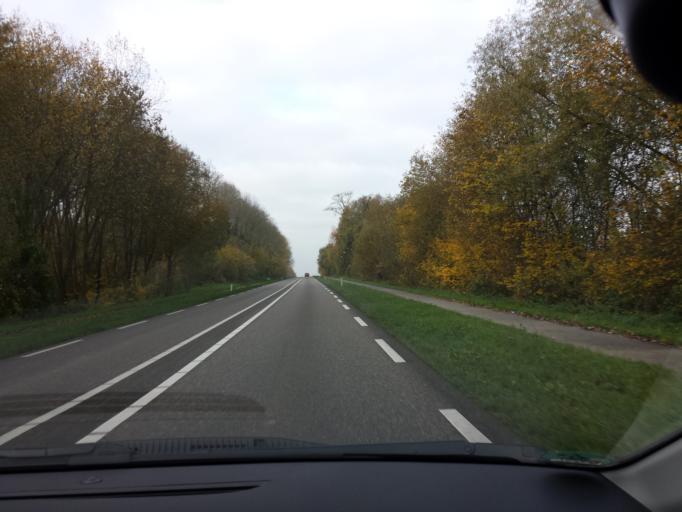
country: NL
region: Limburg
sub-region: Gemeente Simpelveld
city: Simpelveld
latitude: 50.8084
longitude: 5.9508
